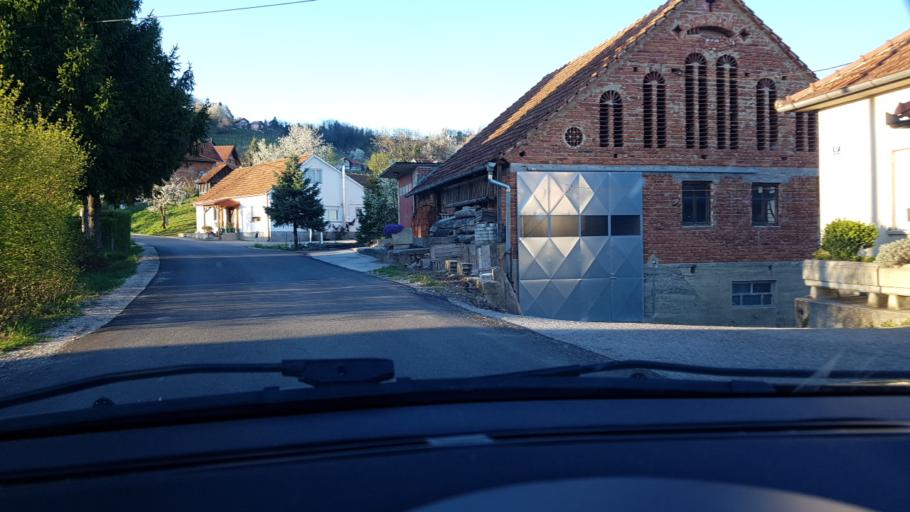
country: HR
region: Krapinsko-Zagorska
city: Pregrada
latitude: 46.1614
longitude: 15.7099
